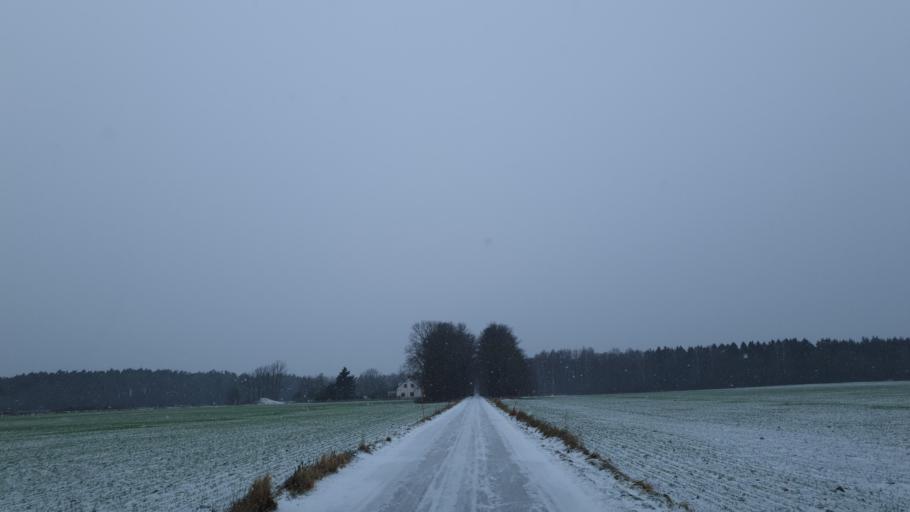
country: SE
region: Gotland
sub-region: Gotland
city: Visby
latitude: 57.5186
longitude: 18.4555
